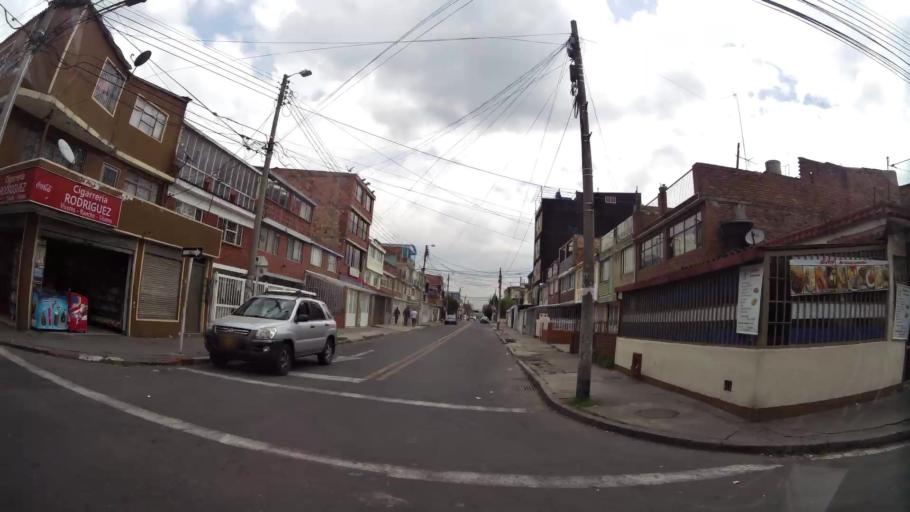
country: CO
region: Bogota D.C.
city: Bogota
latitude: 4.6044
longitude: -74.1085
